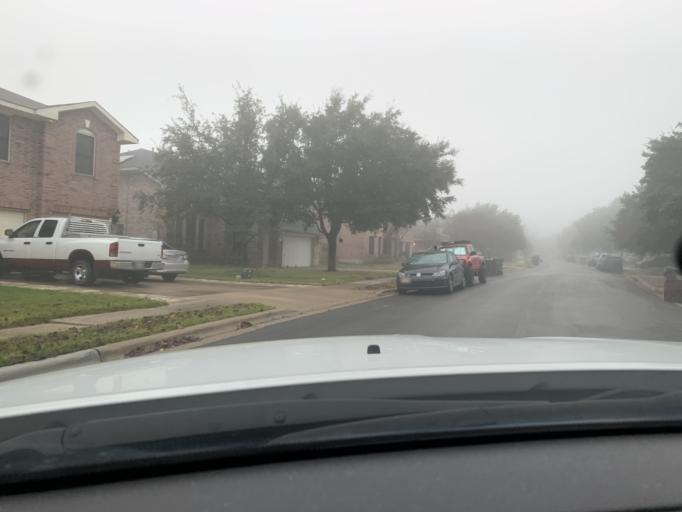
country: US
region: Texas
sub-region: Williamson County
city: Round Rock
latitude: 30.5649
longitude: -97.6640
